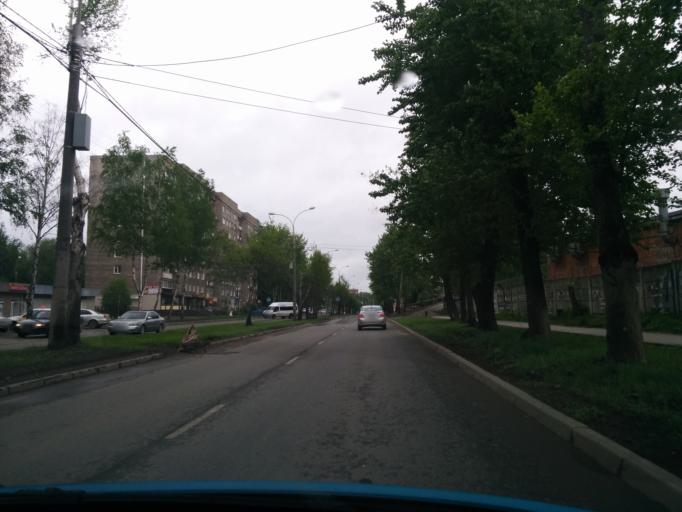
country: RU
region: Perm
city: Perm
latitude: 58.0133
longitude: 56.2935
